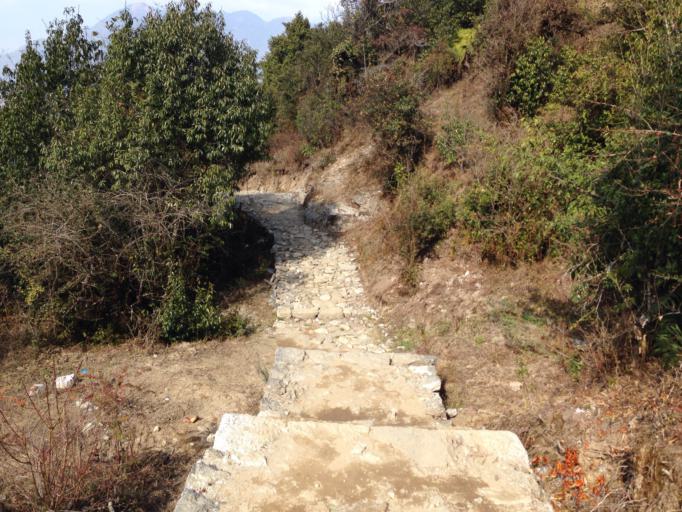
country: NP
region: Central Region
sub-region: Bagmati Zone
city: Nagarkot
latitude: 27.8201
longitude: 85.4467
